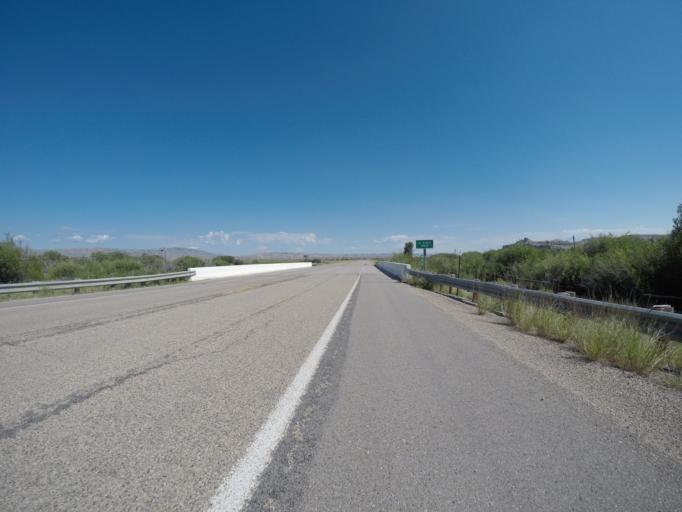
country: US
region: Wyoming
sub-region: Sublette County
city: Marbleton
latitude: 42.2273
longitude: -110.1921
